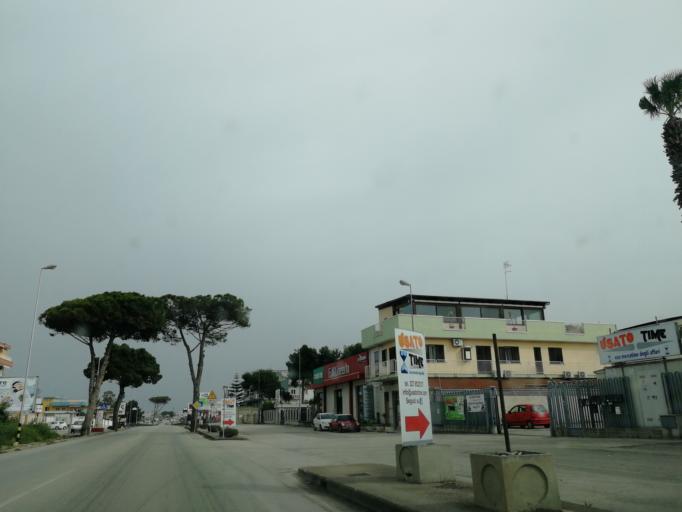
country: IT
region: Apulia
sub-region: Provincia di Barletta - Andria - Trani
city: Barletta
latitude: 41.3119
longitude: 16.3066
